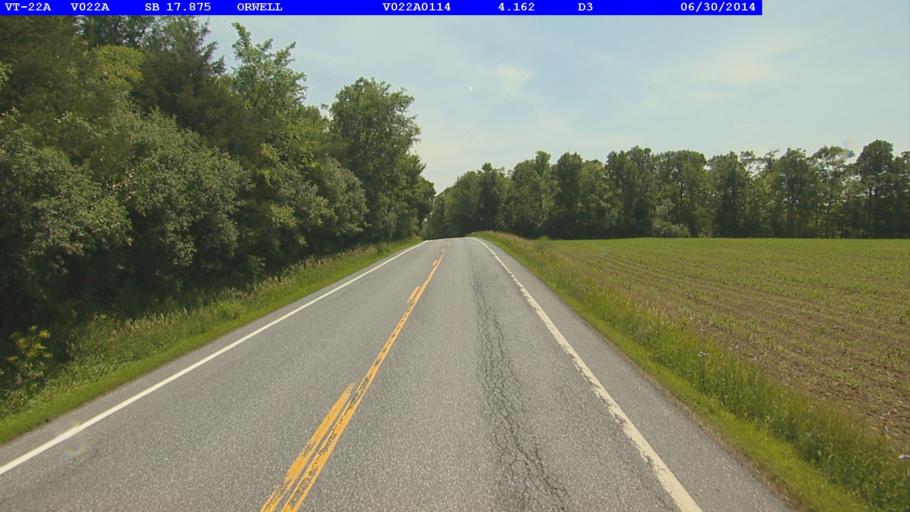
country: US
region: New York
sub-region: Essex County
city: Ticonderoga
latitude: 43.8168
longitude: -73.3059
